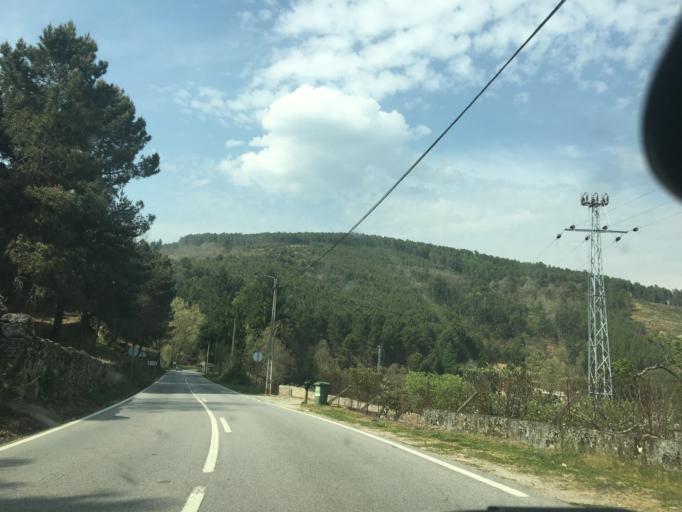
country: PT
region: Vila Real
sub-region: Boticas
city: Boticas
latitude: 41.6870
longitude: -7.6908
